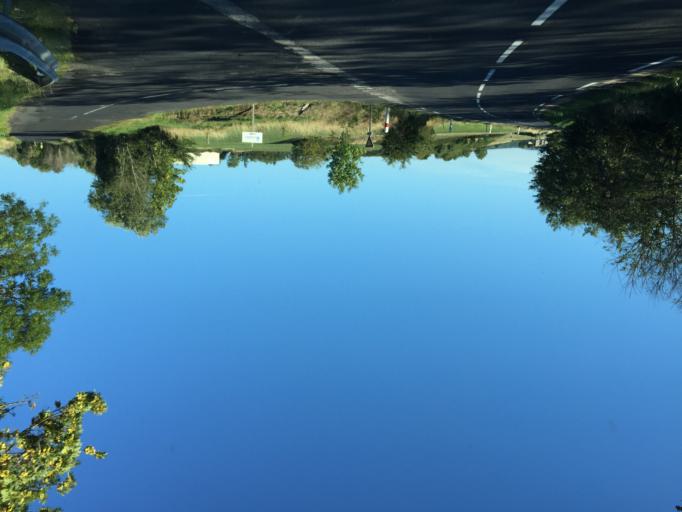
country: FR
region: Auvergne
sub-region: Departement de la Haute-Loire
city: Espaly-Saint-Marcel
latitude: 45.0354
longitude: 3.8651
